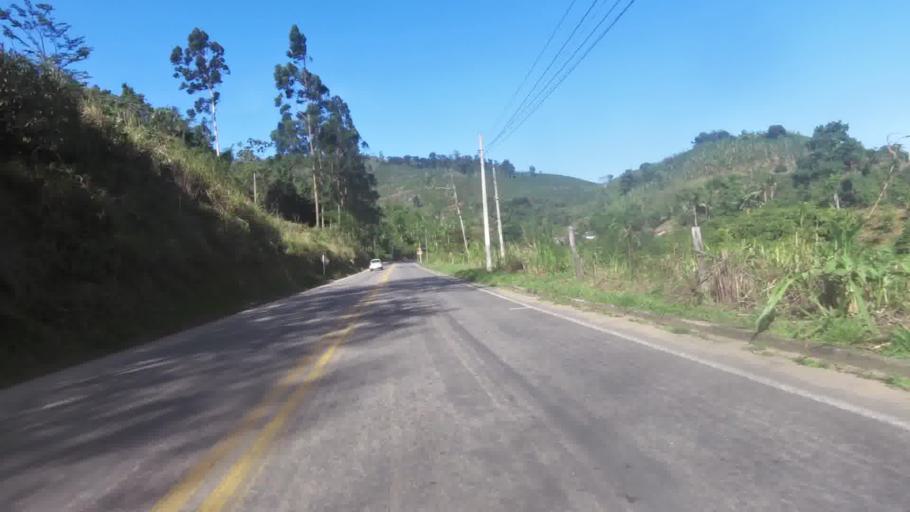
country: BR
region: Espirito Santo
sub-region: Iconha
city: Iconha
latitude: -20.7531
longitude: -40.8392
